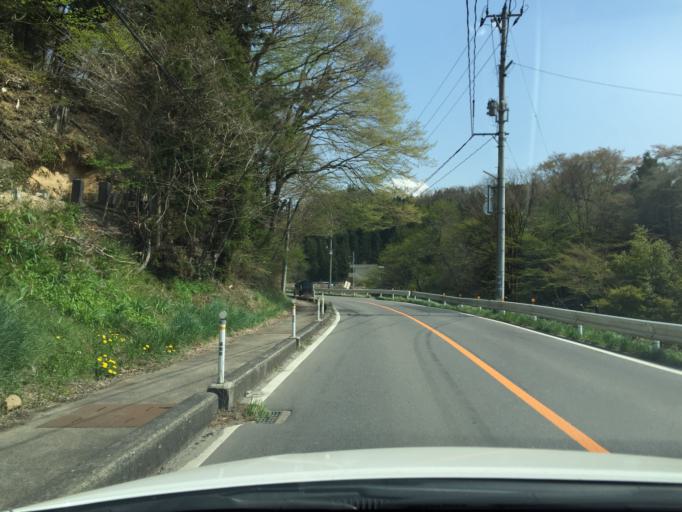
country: JP
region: Fukushima
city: Funehikimachi-funehiki
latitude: 37.4373
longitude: 140.6502
